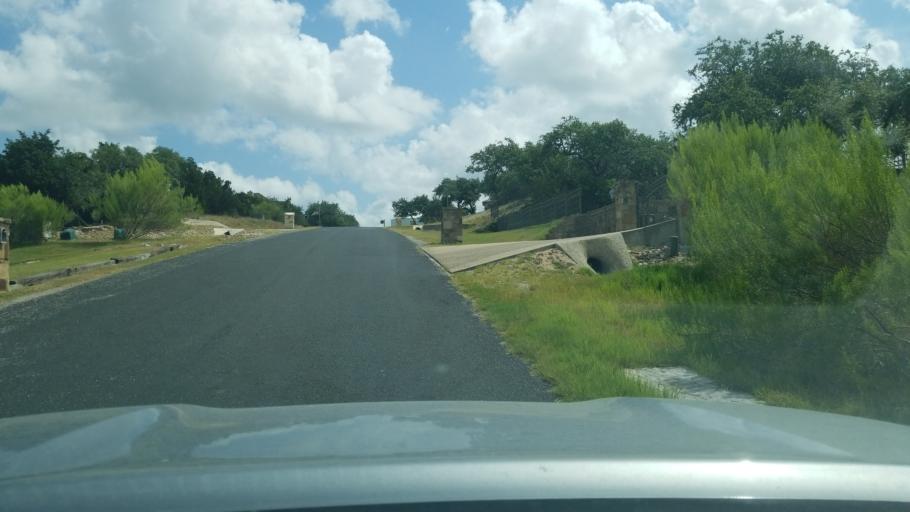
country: US
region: Texas
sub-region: Bexar County
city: Timberwood Park
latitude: 29.6788
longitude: -98.5175
